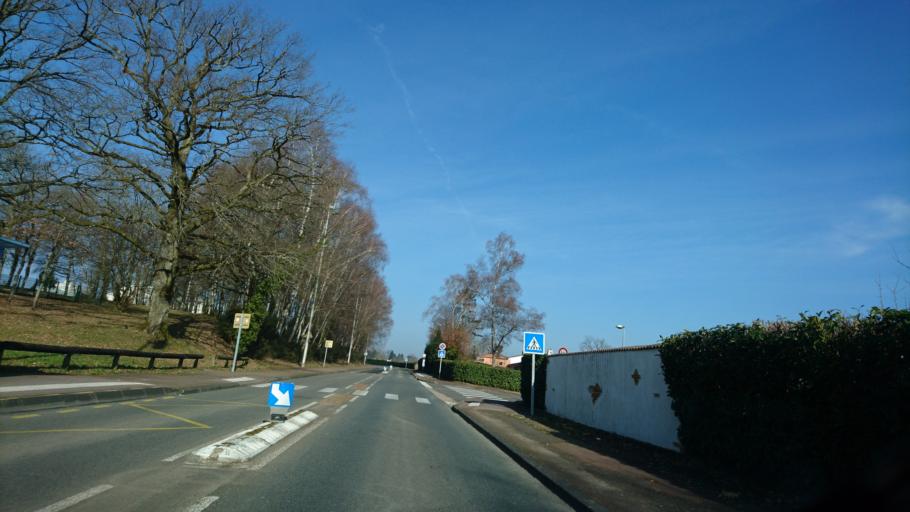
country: FR
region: Limousin
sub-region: Departement de la Haute-Vienne
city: Rilhac-Rancon
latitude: 45.8815
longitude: 1.2994
